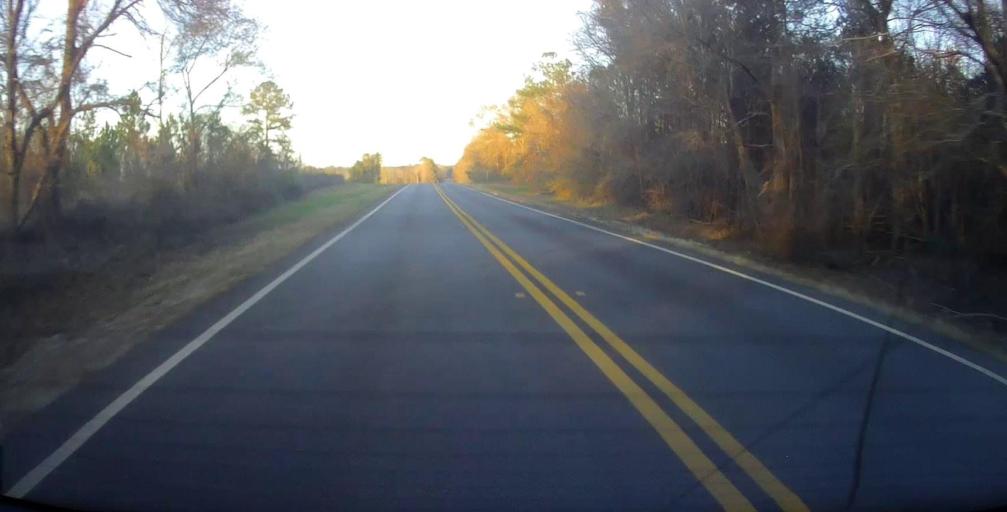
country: US
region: Georgia
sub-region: Dodge County
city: Chester
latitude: 32.3112
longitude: -83.0650
